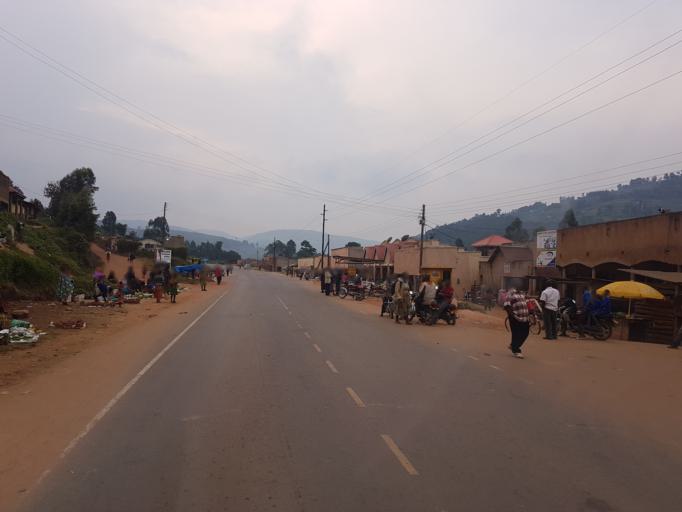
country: UG
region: Western Region
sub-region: Kabale District
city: Kabale
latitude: -1.2188
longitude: 29.9486
